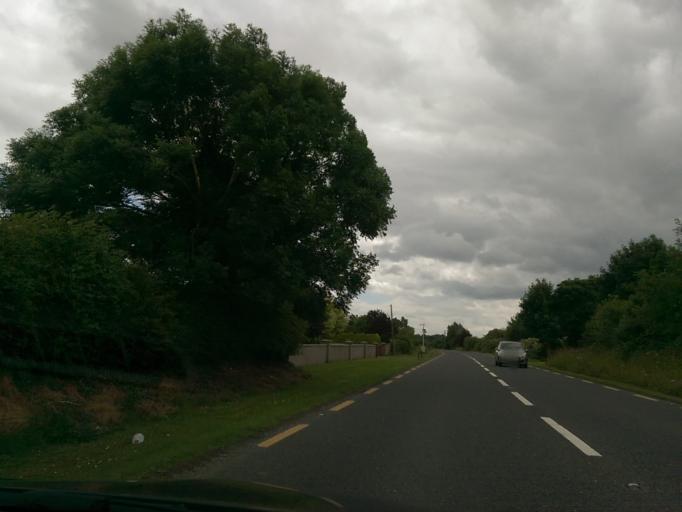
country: IE
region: Munster
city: Thurles
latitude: 52.6406
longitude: -7.7857
